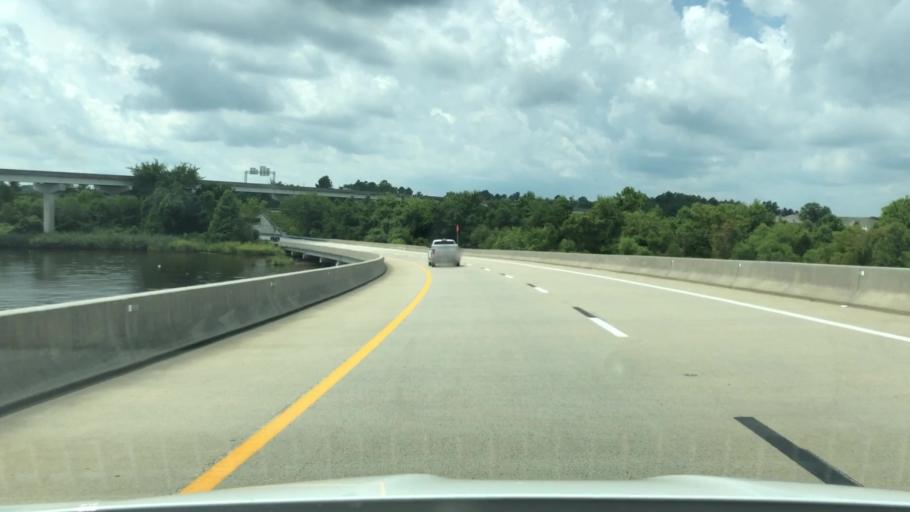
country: US
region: North Carolina
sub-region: Craven County
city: James City
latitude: 35.0965
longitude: -77.0360
